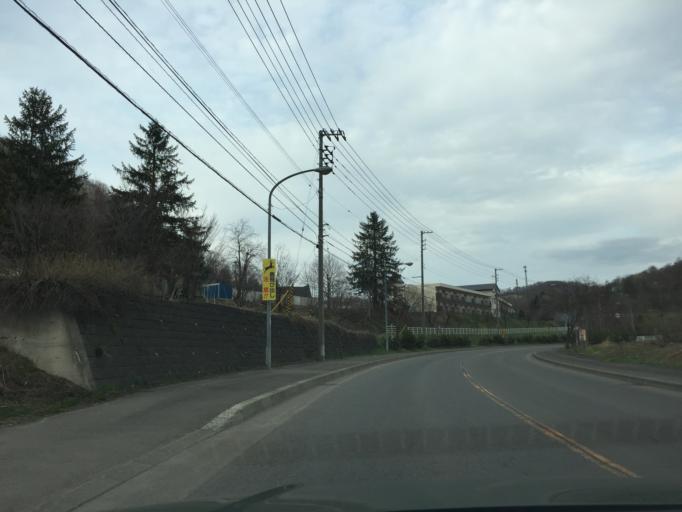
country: JP
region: Hokkaido
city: Utashinai
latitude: 43.5052
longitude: 142.0151
